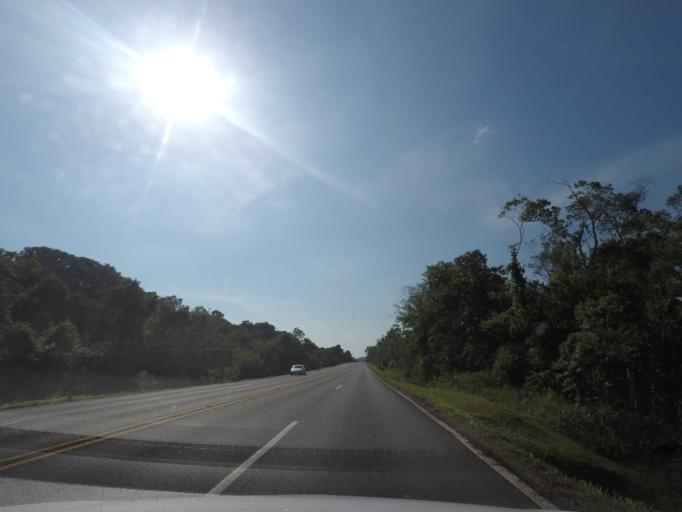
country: BR
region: Parana
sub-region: Paranagua
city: Paranagua
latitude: -25.5927
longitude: -48.6110
